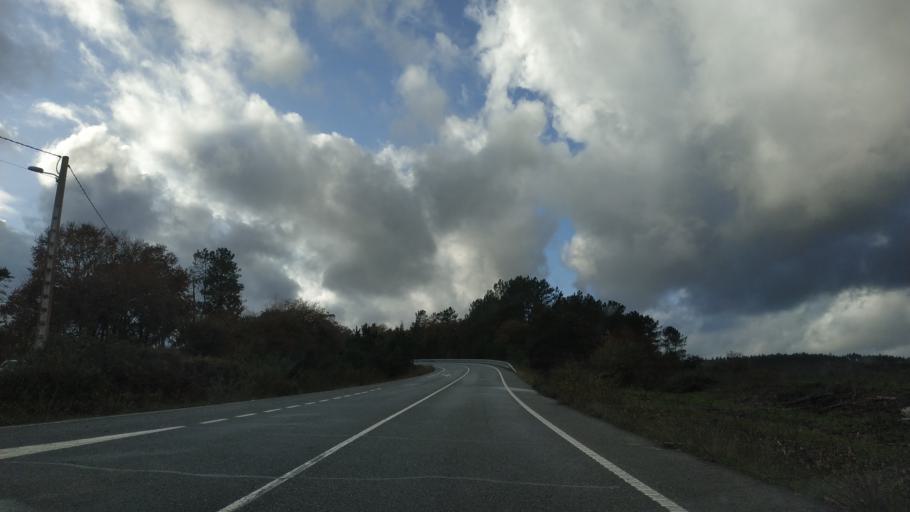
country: ES
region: Galicia
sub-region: Provincia da Coruna
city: Arzua
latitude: 42.8829
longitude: -8.1934
